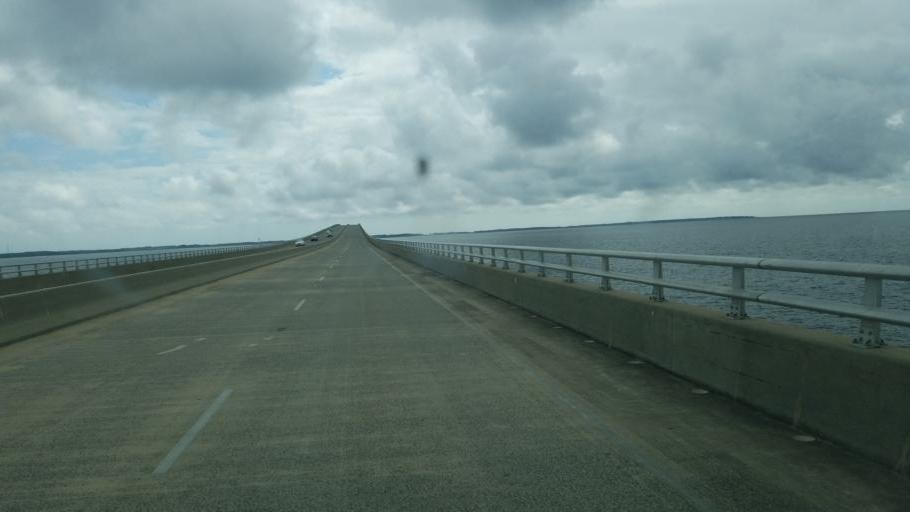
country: US
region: North Carolina
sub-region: Dare County
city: Manteo
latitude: 35.8864
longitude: -75.7275
